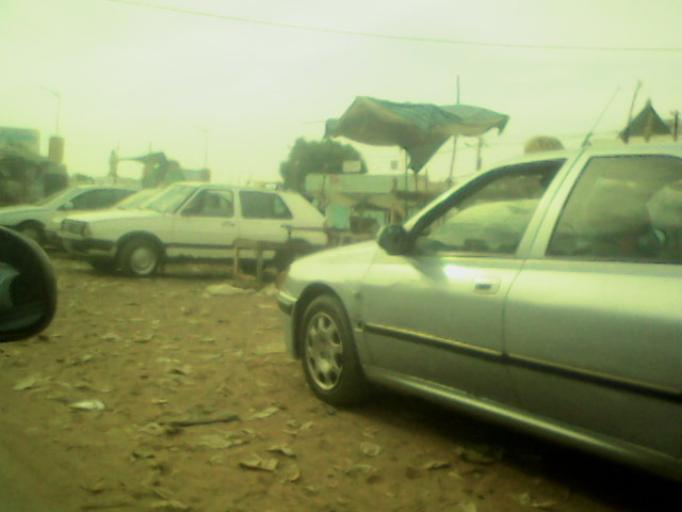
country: SN
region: Diourbel
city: Touba
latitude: 14.8810
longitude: -15.8920
